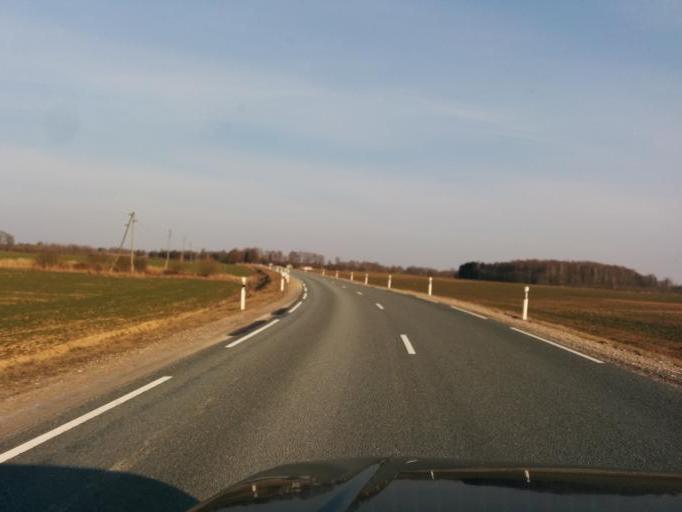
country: LV
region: Lecava
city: Iecava
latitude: 56.5899
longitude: 24.1368
